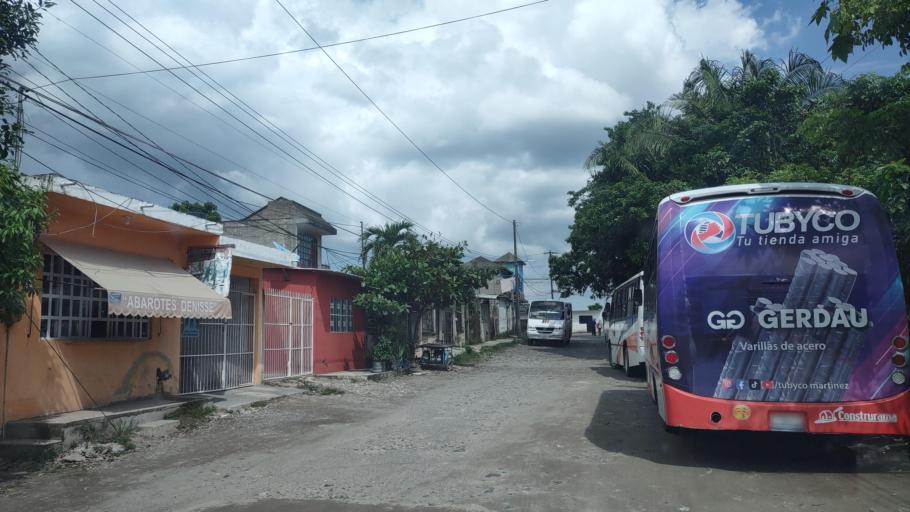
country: MX
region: Veracruz
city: Martinez de la Torre
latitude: 20.0743
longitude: -97.0779
